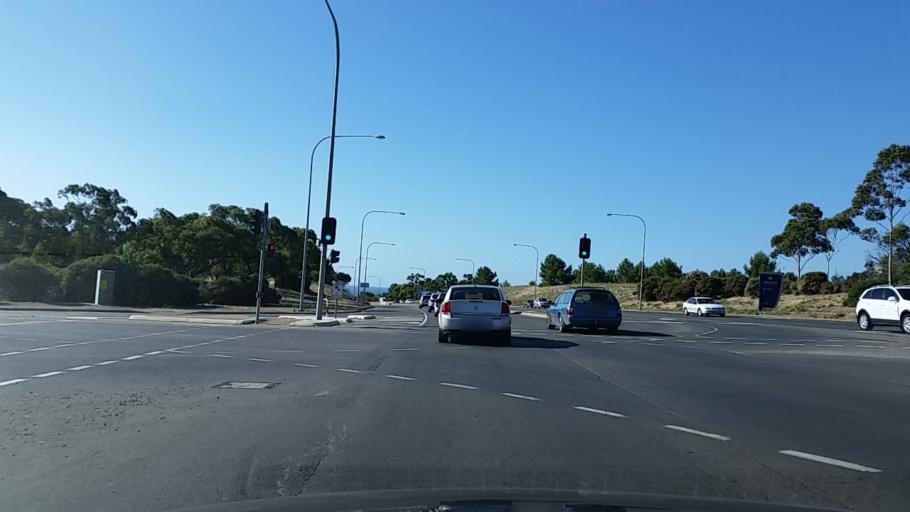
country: AU
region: South Australia
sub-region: Onkaparinga
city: Reynella
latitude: -35.1022
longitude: 138.4997
